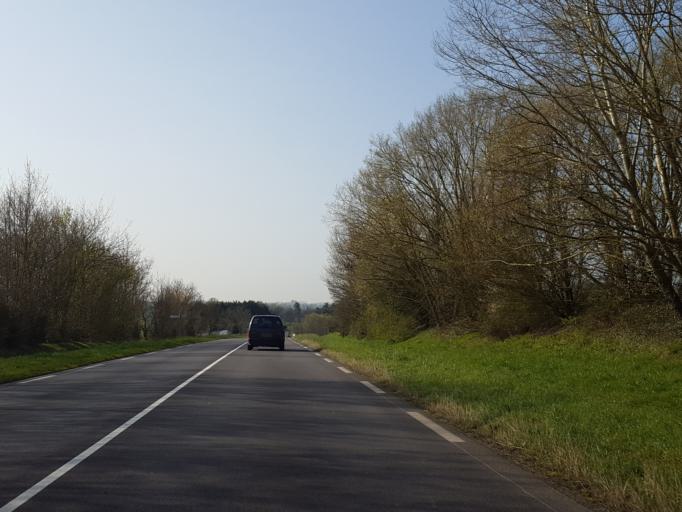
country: FR
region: Pays de la Loire
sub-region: Departement de la Vendee
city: Saint-Philbert-de-Bouaine
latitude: 46.9893
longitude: -1.5164
